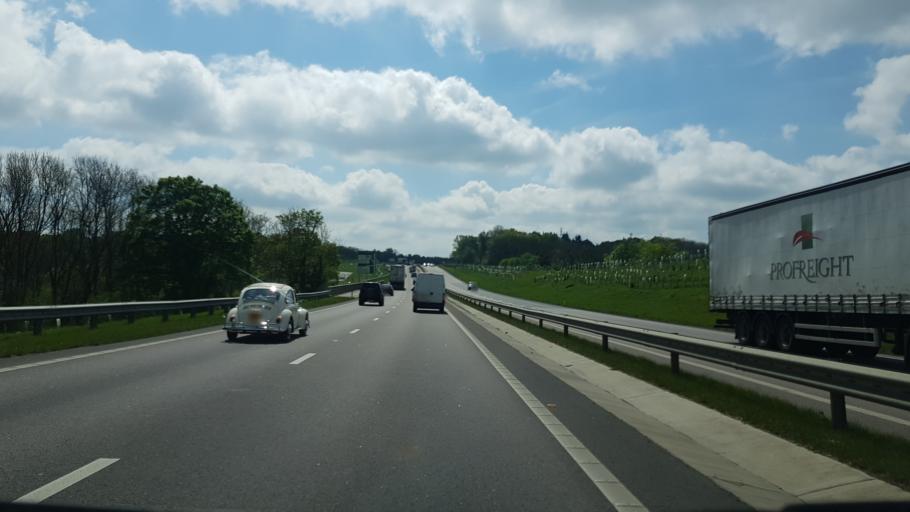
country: GB
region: England
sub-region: Kent
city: Pembury
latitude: 51.1713
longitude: 0.3025
